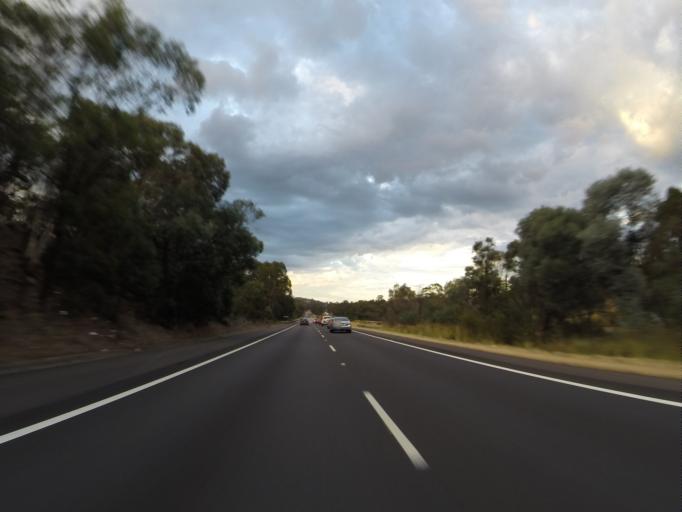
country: AU
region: New South Wales
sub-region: Wollondilly
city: Douglas Park
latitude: -34.1940
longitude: 150.7104
